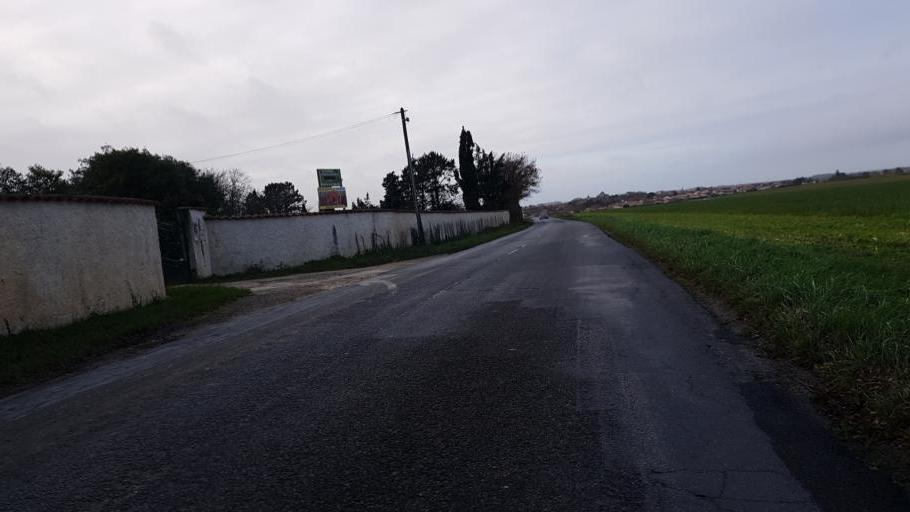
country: FR
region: Poitou-Charentes
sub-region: Departement de la Vienne
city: Avanton
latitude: 46.6610
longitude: 0.3252
